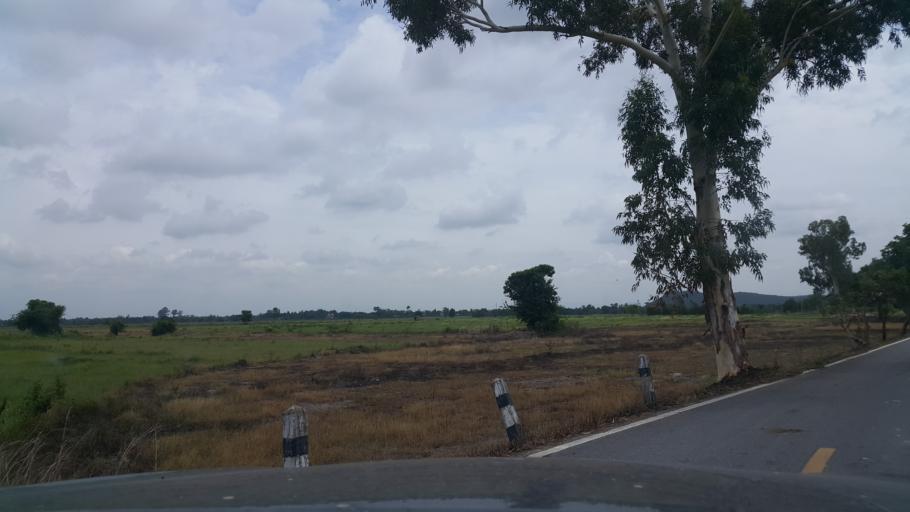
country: TH
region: Lamphun
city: Ban Thi
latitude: 18.6470
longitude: 99.1461
